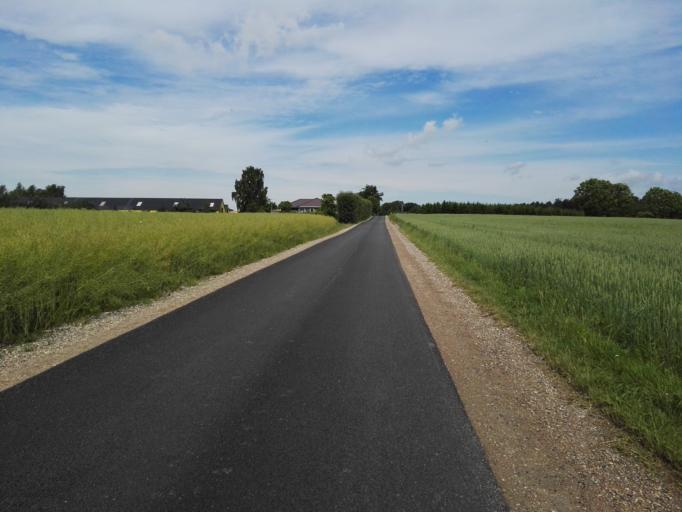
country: DK
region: Capital Region
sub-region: Egedal Kommune
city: Olstykke
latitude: 55.8126
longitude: 12.1775
